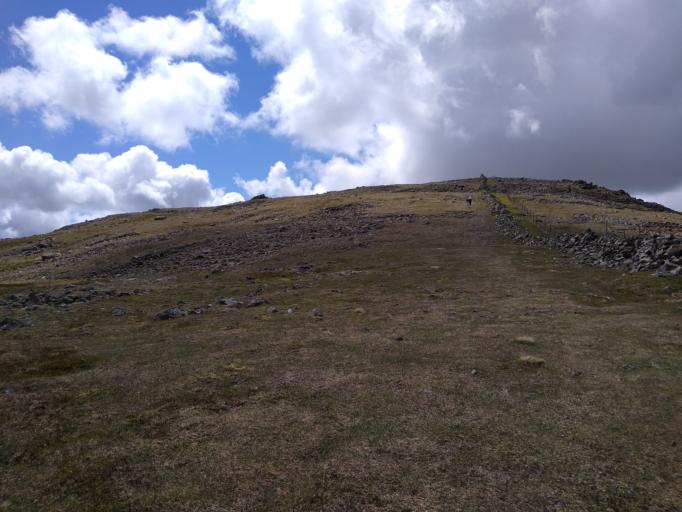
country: GB
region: England
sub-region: Cumbria
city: Cockermouth
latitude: 54.4857
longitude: -3.3189
